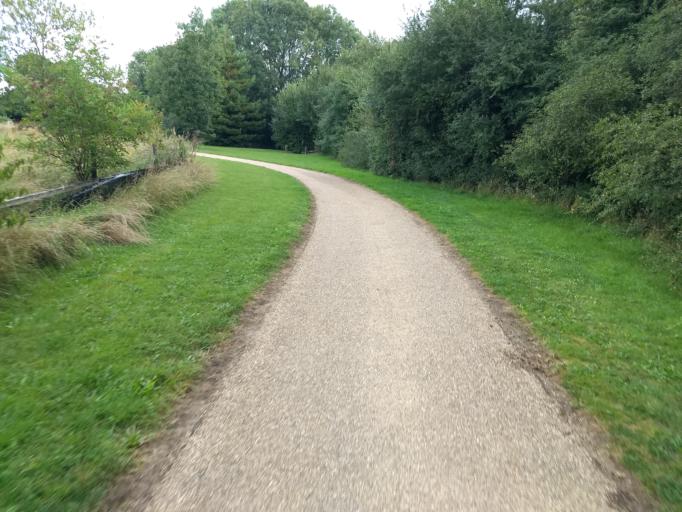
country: GB
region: England
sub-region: Buckinghamshire
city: Newton Longville
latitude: 51.9872
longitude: -0.8031
